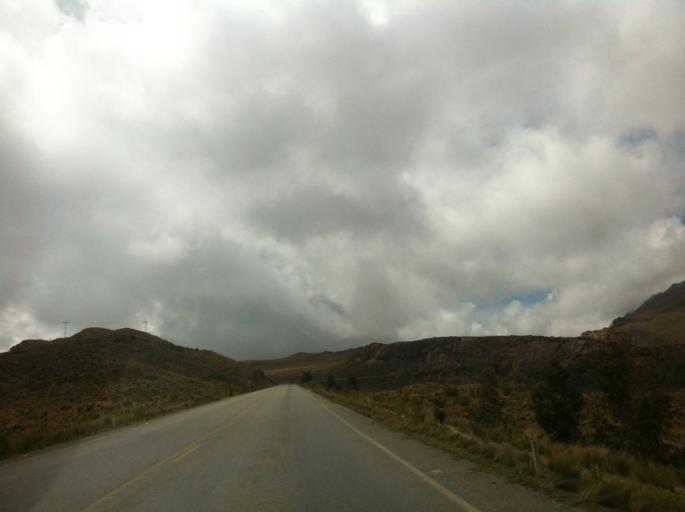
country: BO
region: Cochabamba
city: Irpa Irpa
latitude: -17.6864
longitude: -66.4822
